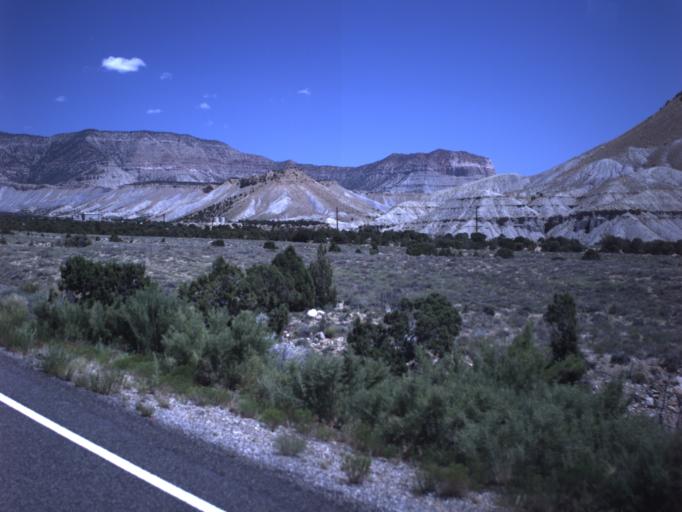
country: US
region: Utah
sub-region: Emery County
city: Orangeville
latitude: 39.2667
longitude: -111.1019
